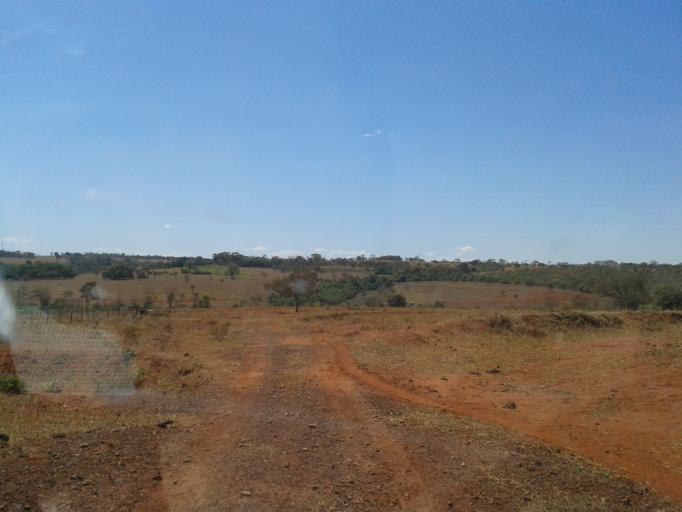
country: BR
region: Minas Gerais
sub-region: Monte Alegre De Minas
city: Monte Alegre de Minas
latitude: -18.8005
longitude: -49.0784
